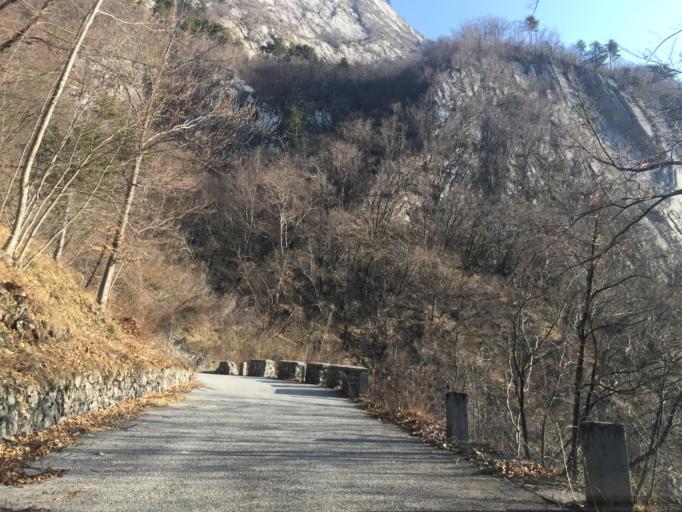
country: IT
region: Friuli Venezia Giulia
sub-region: Provincia di Udine
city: Amaro
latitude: 46.3893
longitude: 13.0762
